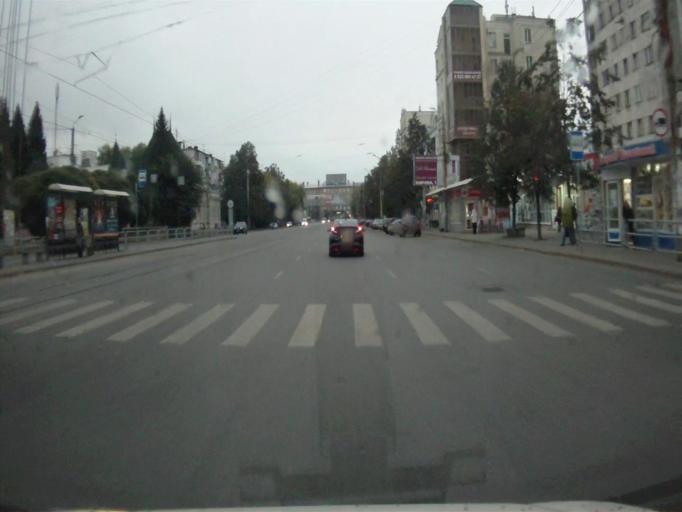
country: RU
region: Chelyabinsk
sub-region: Gorod Chelyabinsk
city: Chelyabinsk
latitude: 55.1795
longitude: 61.3995
